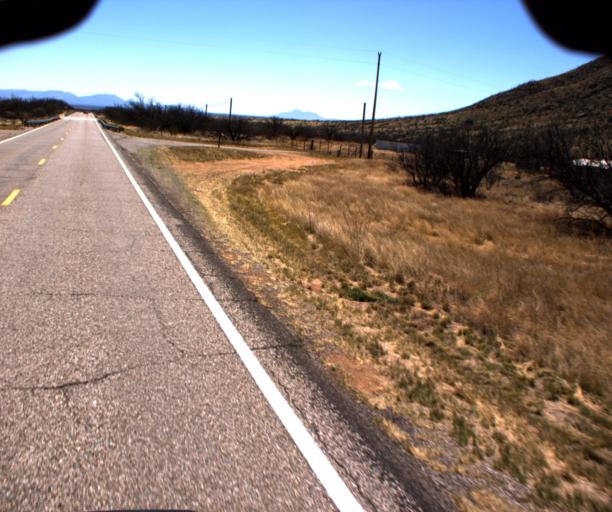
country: US
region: Arizona
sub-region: Cochise County
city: Huachuca City
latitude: 31.7002
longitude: -110.4289
